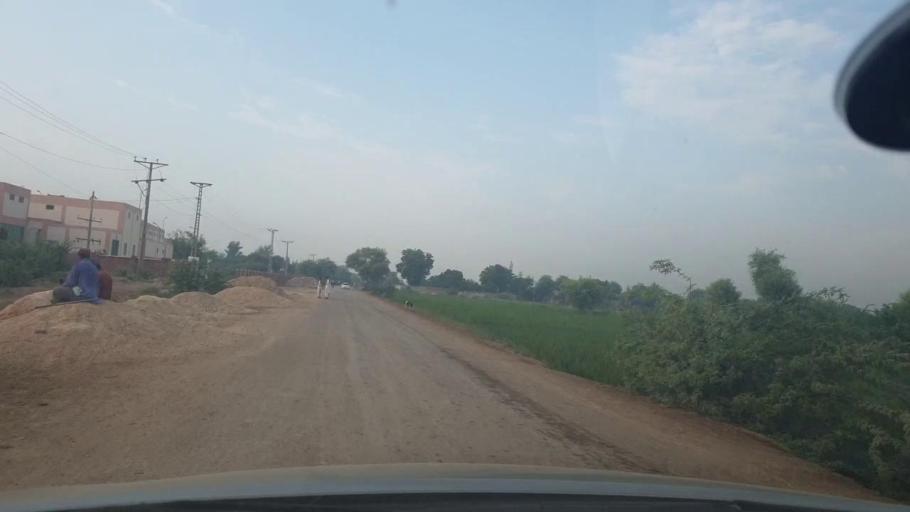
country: PK
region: Sindh
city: Jacobabad
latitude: 28.2757
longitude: 68.4231
